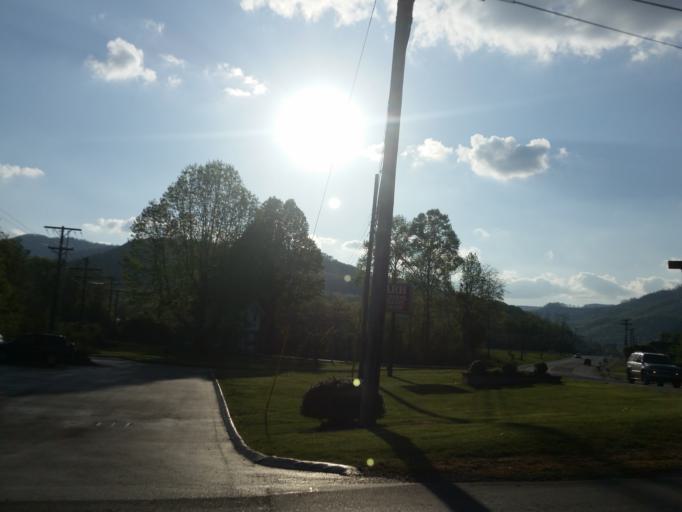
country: US
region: Kentucky
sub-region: Bell County
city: Middlesboro
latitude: 36.6050
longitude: -83.7424
